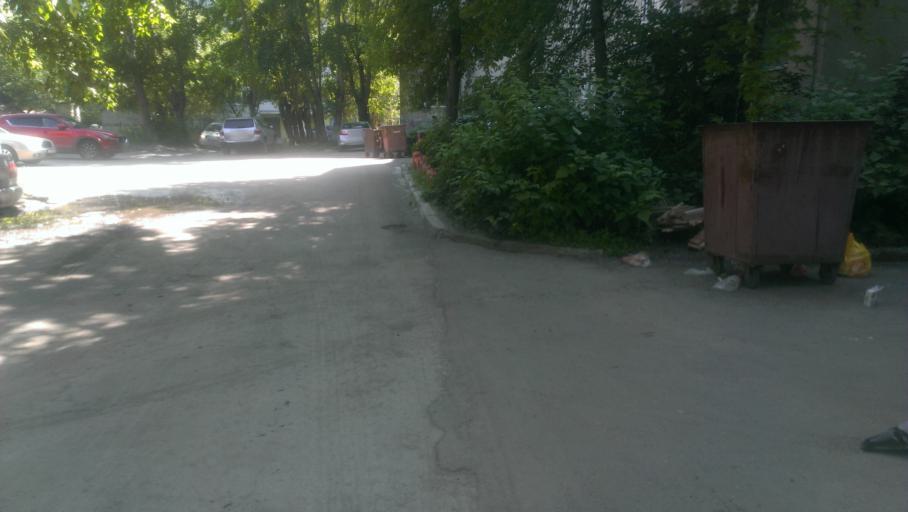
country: RU
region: Altai Krai
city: Novosilikatnyy
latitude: 53.3454
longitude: 83.6807
